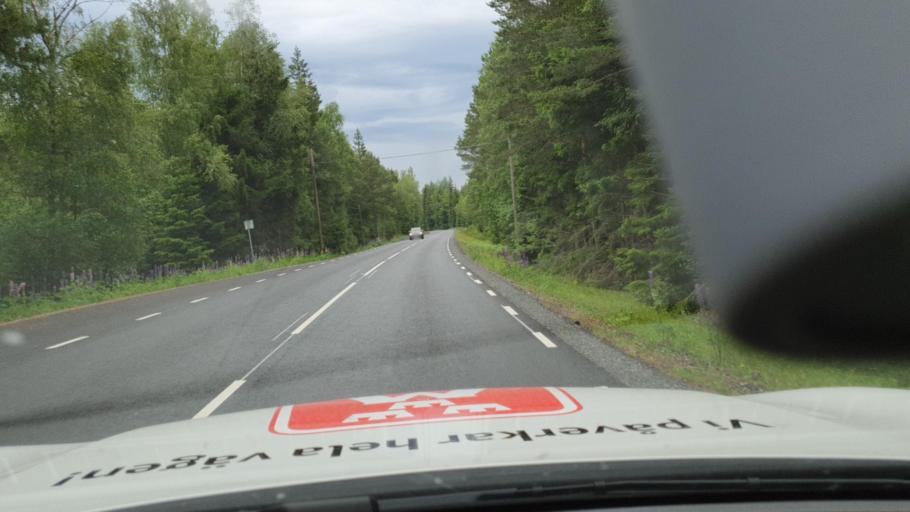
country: SE
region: OErebro
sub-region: Laxa Kommun
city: Laxa
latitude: 58.8846
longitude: 14.4963
